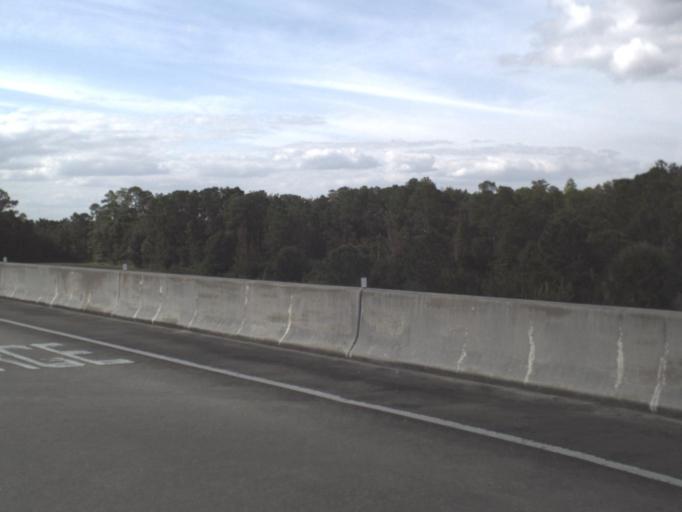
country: US
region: Florida
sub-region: Osceola County
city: Celebration
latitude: 28.3458
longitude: -81.5334
